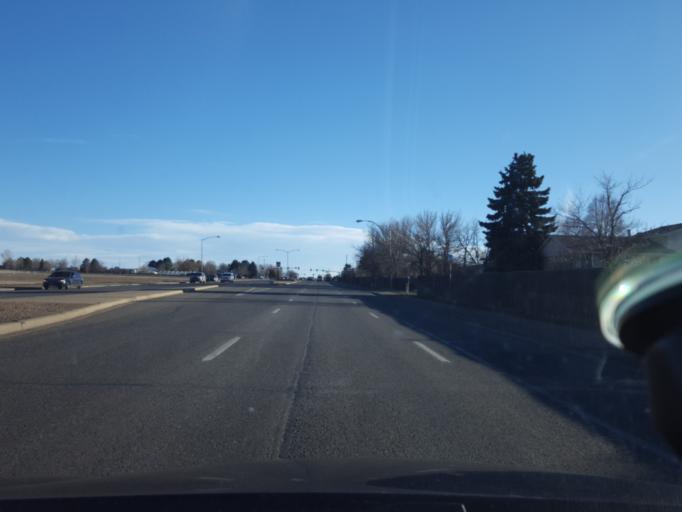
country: US
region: Colorado
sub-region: Adams County
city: Aurora
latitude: 39.7288
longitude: -104.7913
